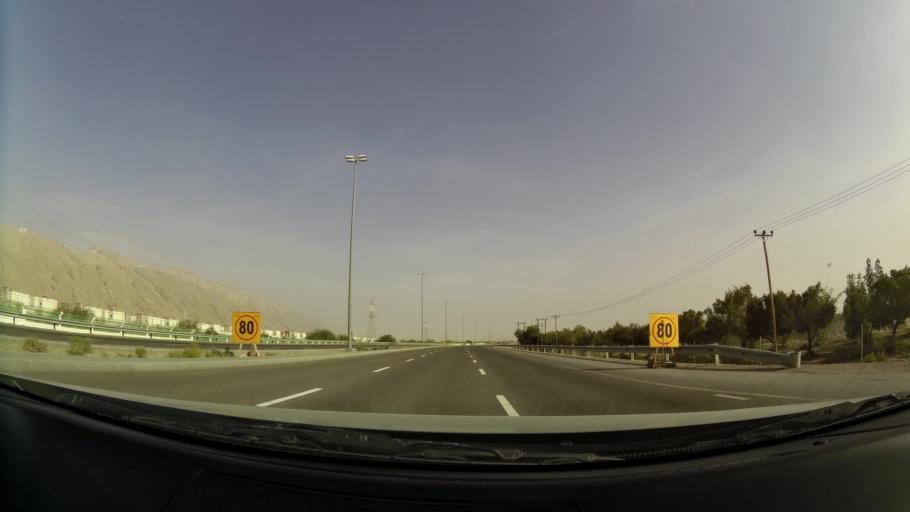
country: AE
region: Abu Dhabi
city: Al Ain
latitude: 24.0871
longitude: 55.7249
